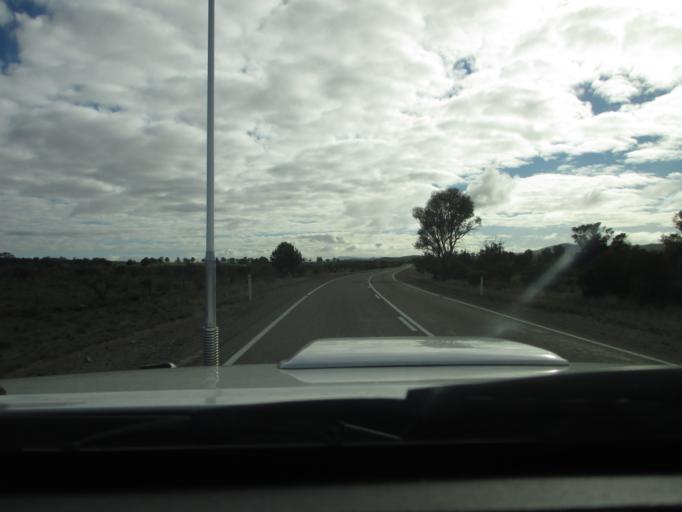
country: AU
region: South Australia
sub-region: Flinders Ranges
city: Quorn
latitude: -32.5075
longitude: 138.5465
